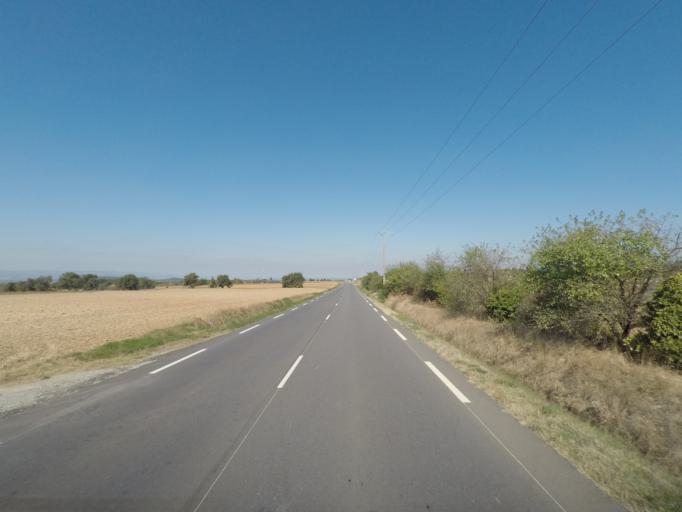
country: FR
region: Rhone-Alpes
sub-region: Departement de la Drome
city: Upie
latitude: 44.8126
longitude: 5.0122
